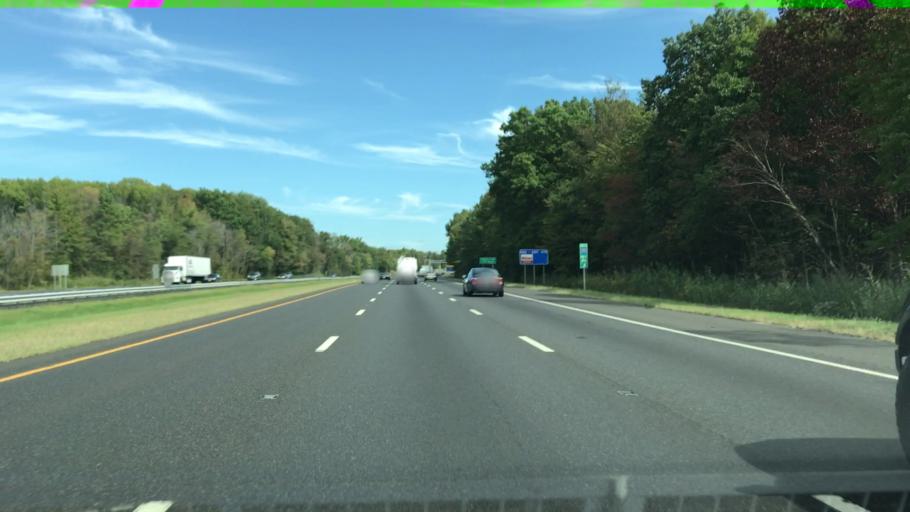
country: US
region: New Jersey
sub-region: Burlington County
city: Willingboro
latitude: 40.0374
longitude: -74.8385
